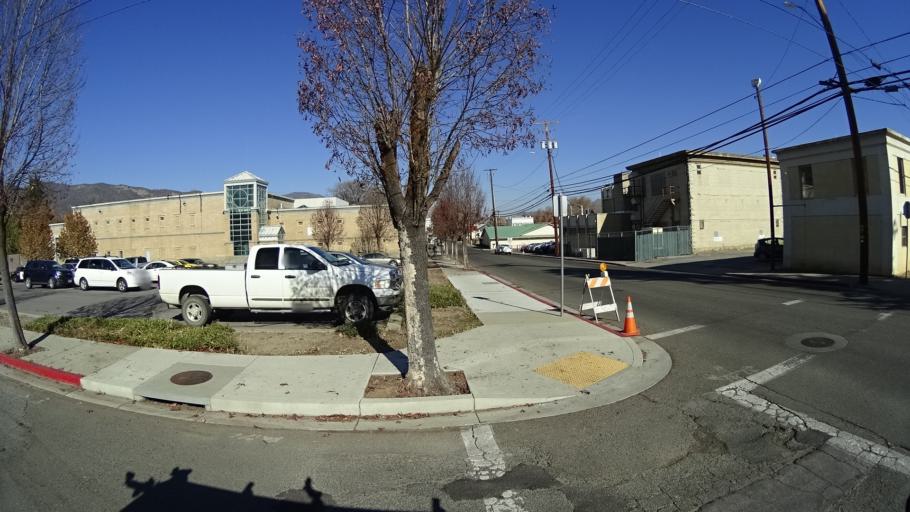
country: US
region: California
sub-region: Siskiyou County
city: Yreka
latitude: 41.7300
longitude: -122.6395
